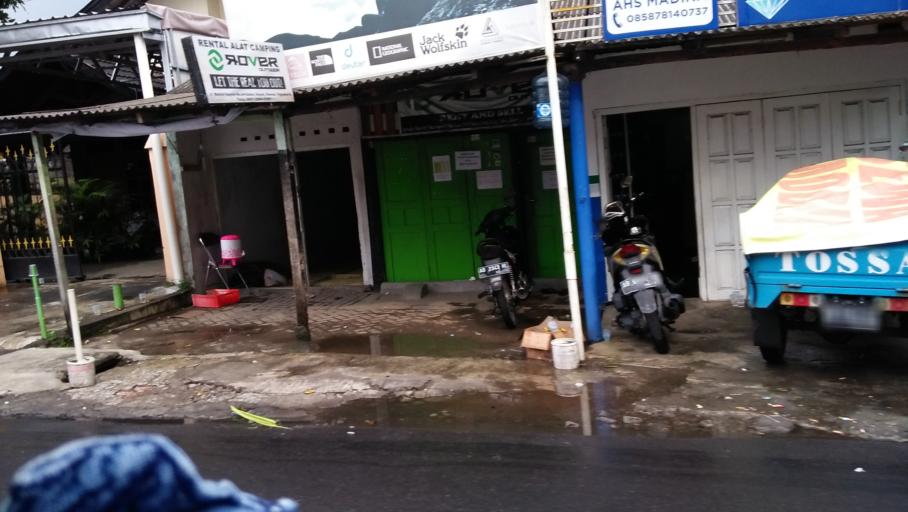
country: ID
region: Daerah Istimewa Yogyakarta
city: Depok
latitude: -7.7726
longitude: 110.4014
